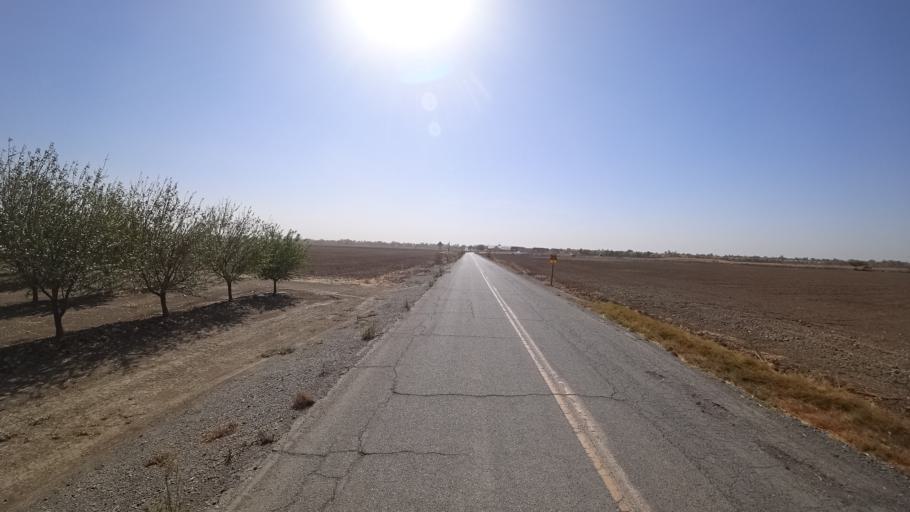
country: US
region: California
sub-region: Yolo County
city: Davis
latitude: 38.5657
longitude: -121.6939
